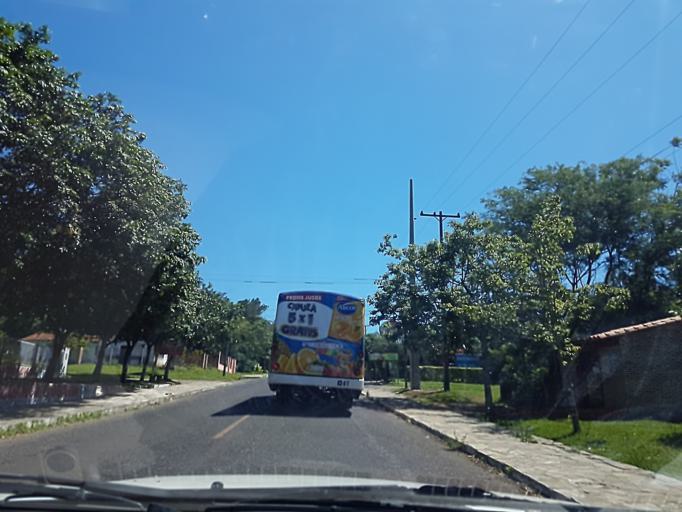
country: PY
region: Cordillera
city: Altos
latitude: -25.2596
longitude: -57.2479
